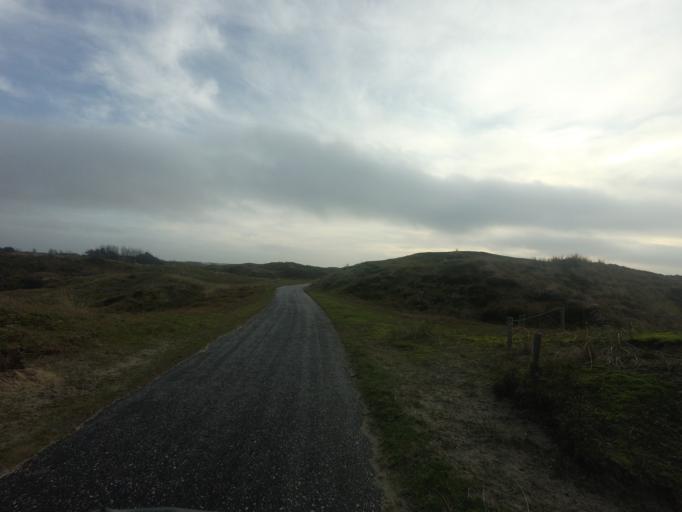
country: NL
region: North Holland
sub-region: Gemeente Texel
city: Den Burg
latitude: 53.1558
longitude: 4.8412
